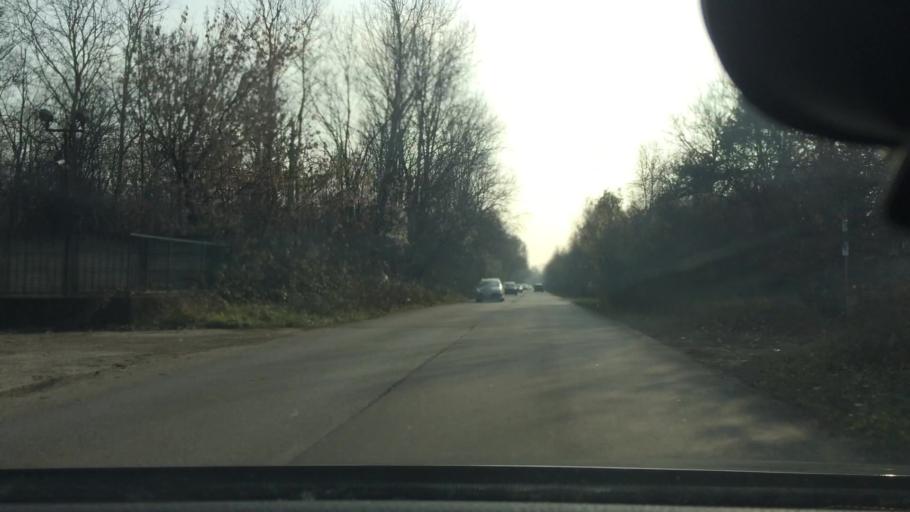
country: IT
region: Lombardy
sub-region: Provincia di Monza e Brianza
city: Villaggio del Sole
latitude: 45.6030
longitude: 9.0960
